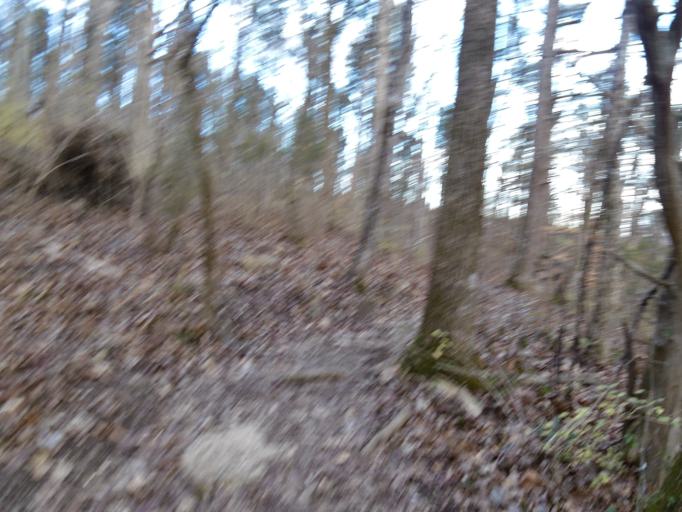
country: US
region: Tennessee
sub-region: Knox County
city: Knoxville
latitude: 35.9492
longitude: -83.8473
